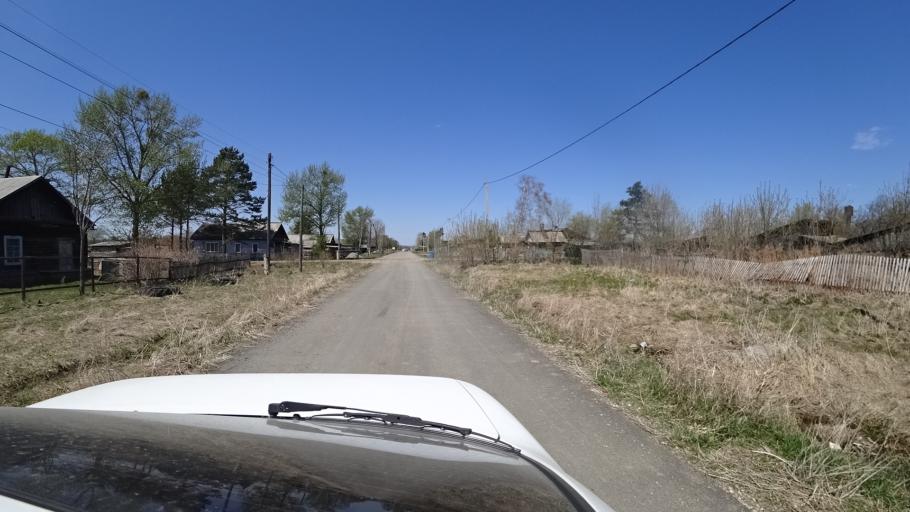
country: RU
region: Primorskiy
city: Dal'nerechensk
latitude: 45.7924
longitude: 133.7725
